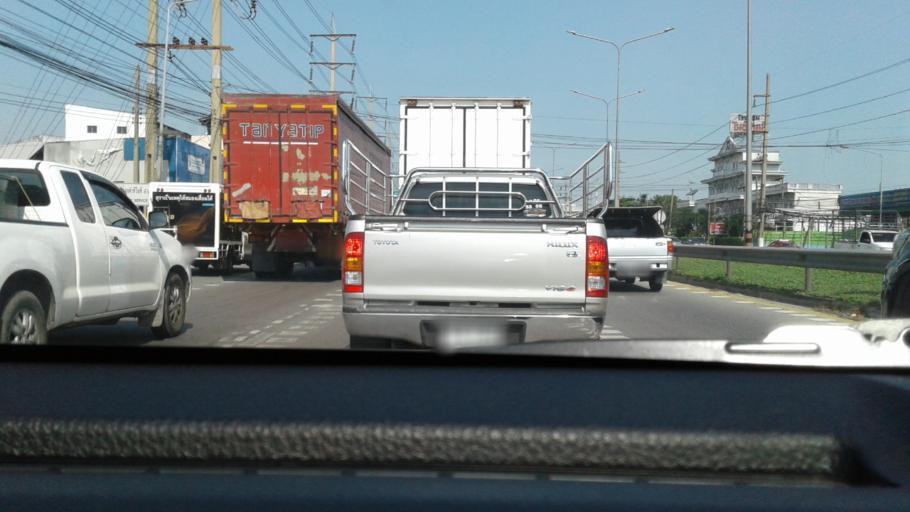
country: TH
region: Phra Nakhon Si Ayutthaya
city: Ban Bang Kadi Pathum Thani
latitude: 13.9812
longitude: 100.5932
